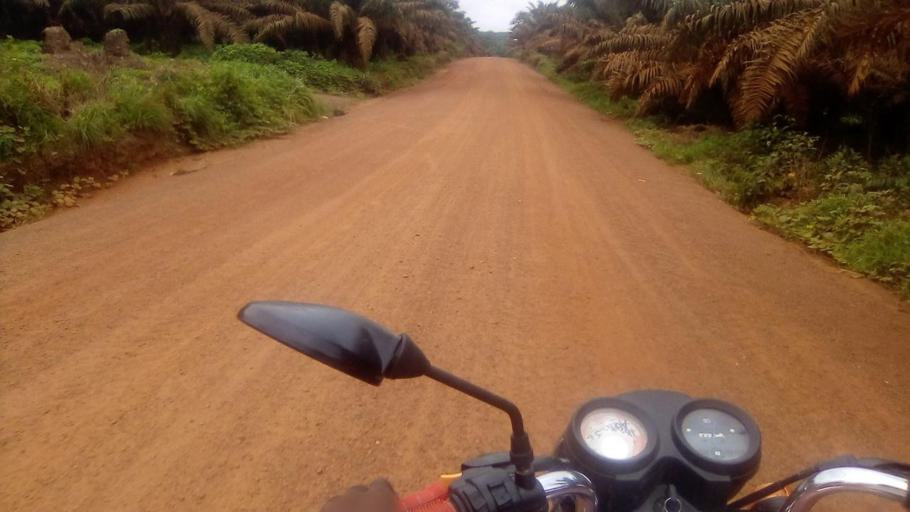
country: SL
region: Southern Province
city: Tongole
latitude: 7.4354
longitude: -11.8600
